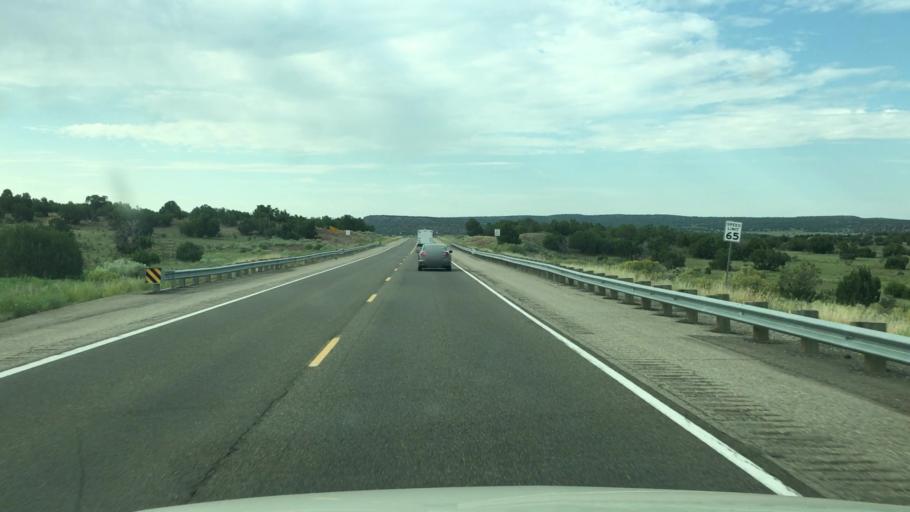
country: US
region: New Mexico
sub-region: Santa Fe County
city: Eldorado at Santa Fe
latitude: 35.2616
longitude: -105.8088
